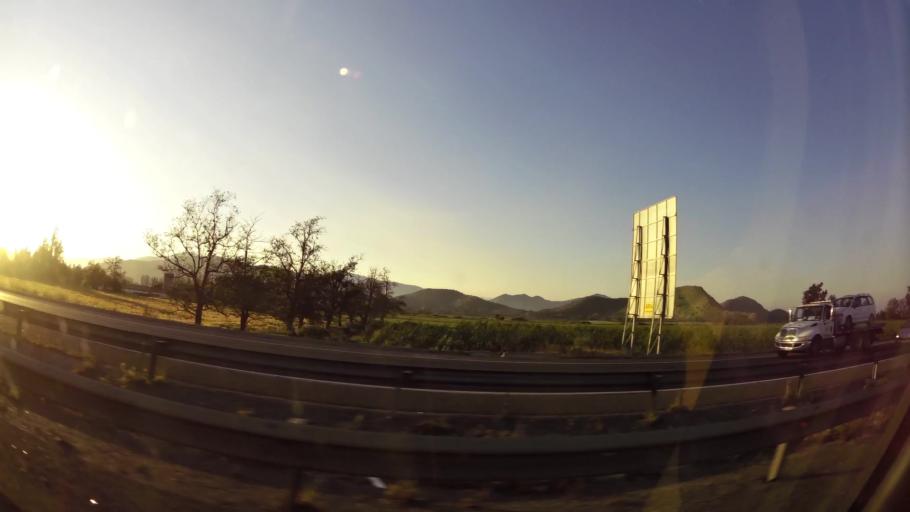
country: CL
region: Santiago Metropolitan
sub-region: Provincia de Talagante
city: Penaflor
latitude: -33.5562
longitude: -70.8209
